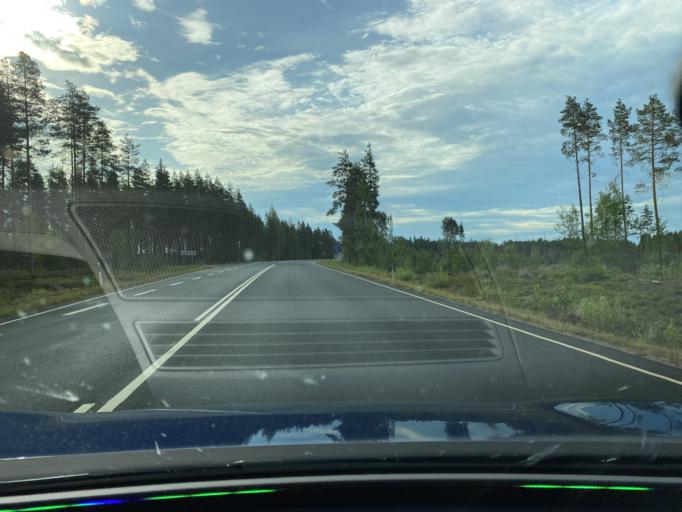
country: FI
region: Central Ostrobothnia
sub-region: Kaustinen
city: Halsua
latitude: 63.4084
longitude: 23.9749
